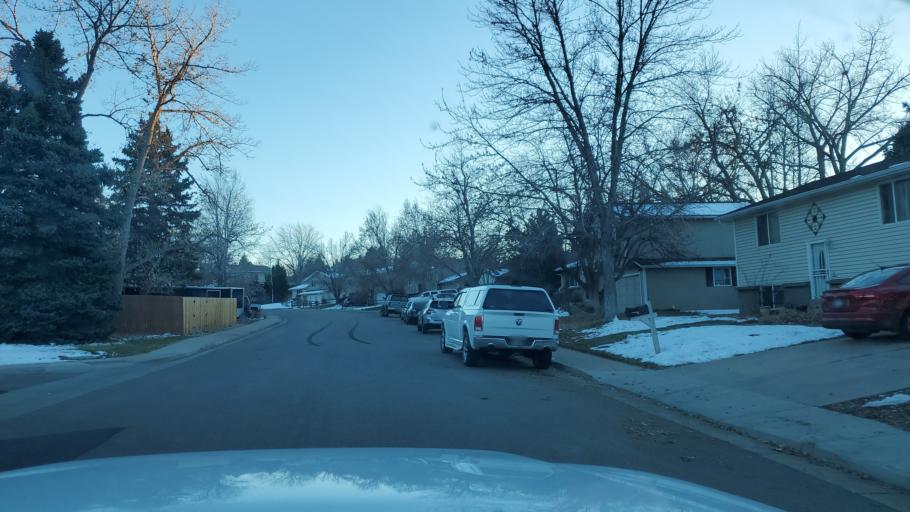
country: US
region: Colorado
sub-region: Arapahoe County
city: Castlewood
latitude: 39.5909
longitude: -104.9035
